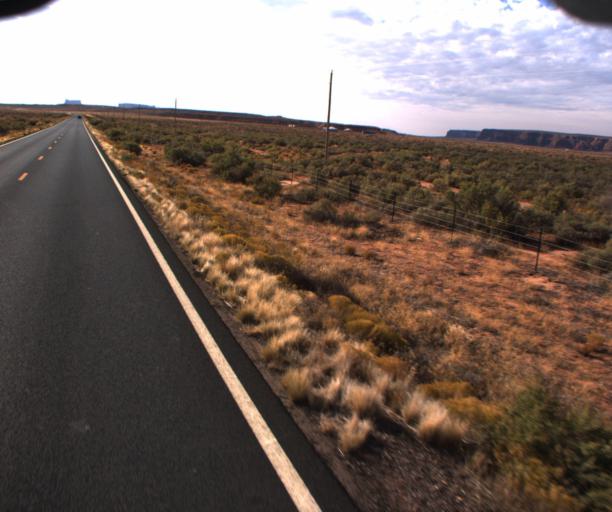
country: US
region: Arizona
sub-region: Apache County
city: Many Farms
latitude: 36.6248
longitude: -109.5830
